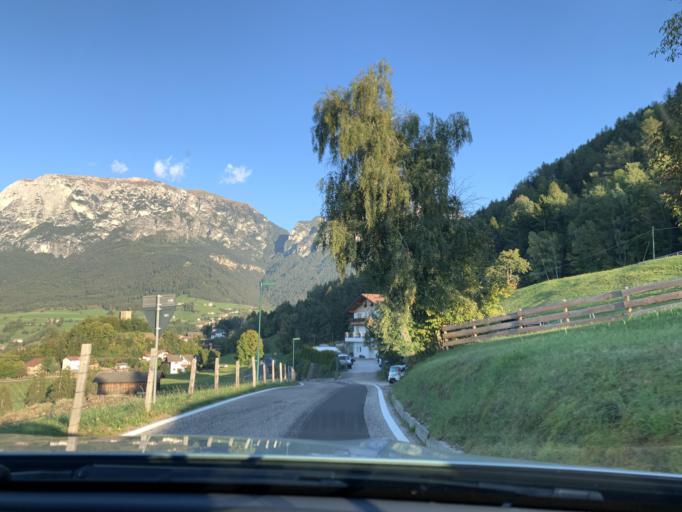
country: IT
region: Trentino-Alto Adige
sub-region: Bolzano
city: Fie Allo Sciliar
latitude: 46.5032
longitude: 11.4899
